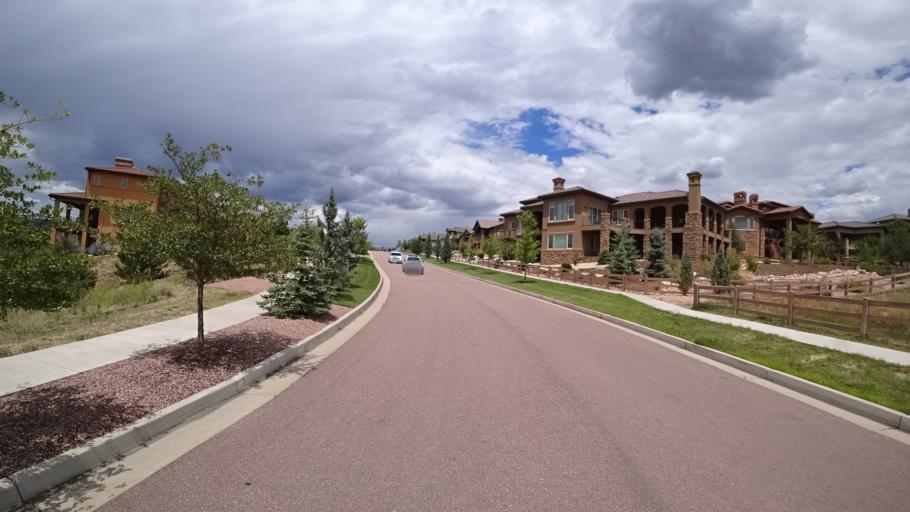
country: US
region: Colorado
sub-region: El Paso County
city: Gleneagle
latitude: 39.0200
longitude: -104.8028
